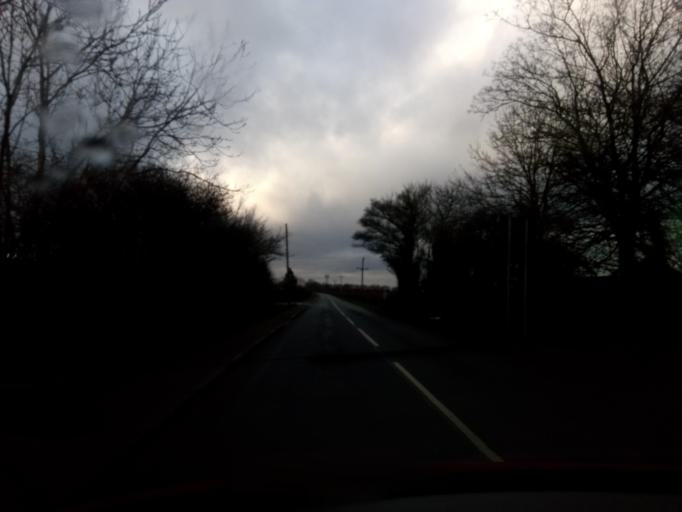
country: GB
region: England
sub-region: Leicestershire
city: Sileby
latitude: 52.7509
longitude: -1.0920
